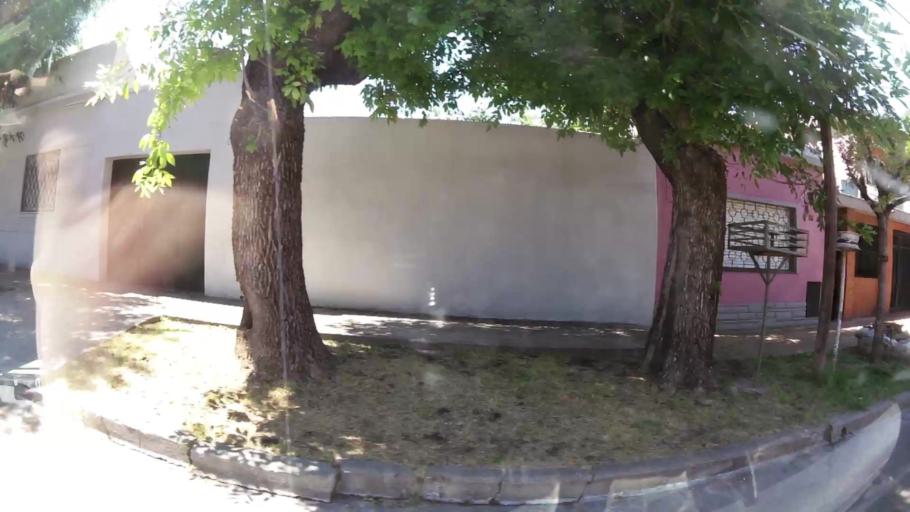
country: AR
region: Buenos Aires
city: Ituzaingo
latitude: -34.6797
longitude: -58.6767
